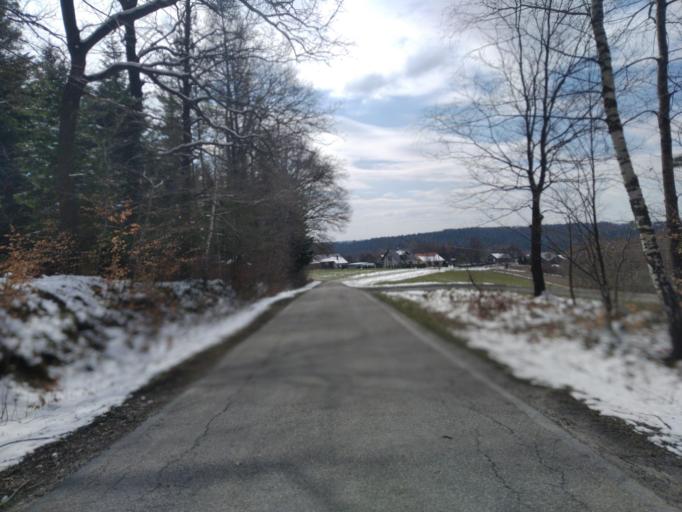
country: PL
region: Subcarpathian Voivodeship
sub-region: Powiat ropczycko-sedziszowski
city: Ropczyce
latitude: 50.0104
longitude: 21.5959
